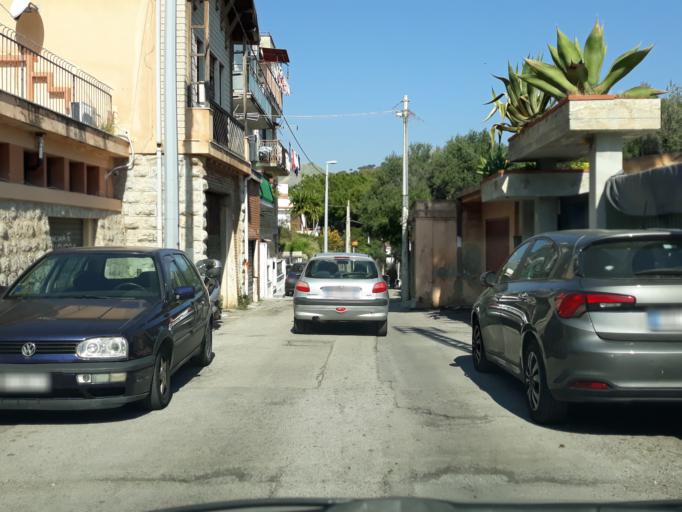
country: IT
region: Sicily
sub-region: Palermo
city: Piano dei Geli
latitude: 38.1125
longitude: 13.2977
